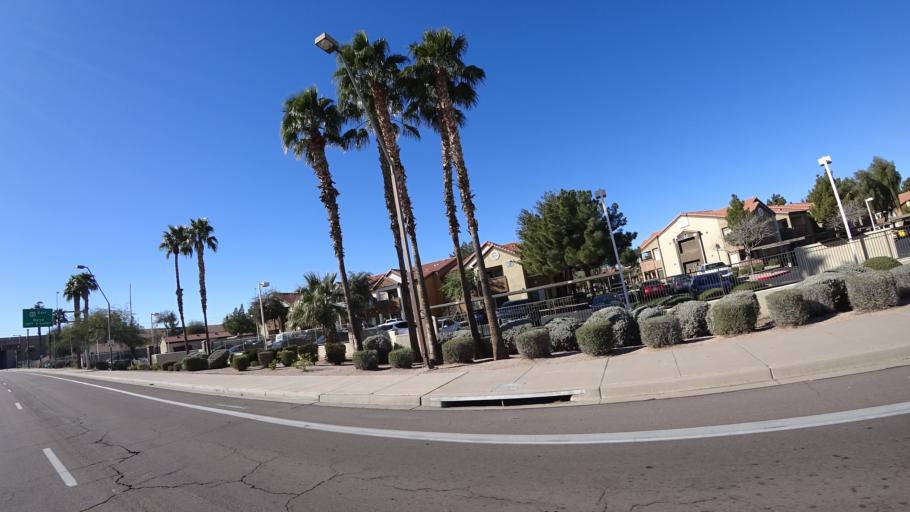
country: US
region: Arizona
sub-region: Maricopa County
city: Guadalupe
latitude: 33.3893
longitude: -111.9610
